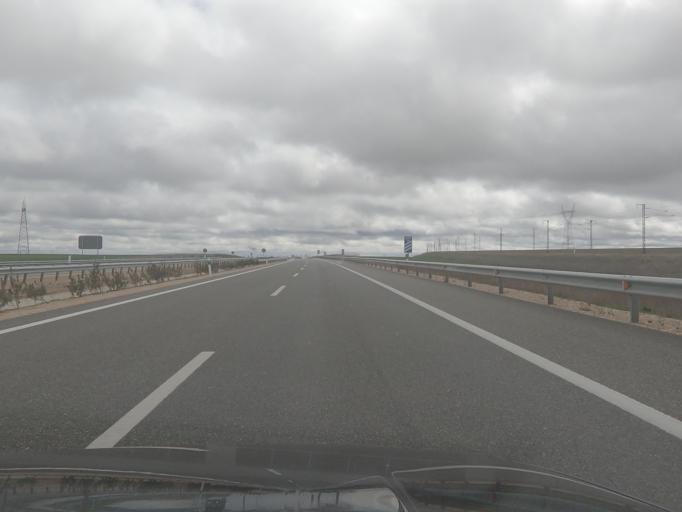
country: ES
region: Castille and Leon
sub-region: Provincia de Zamora
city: Montamarta
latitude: 41.6151
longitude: -5.7874
